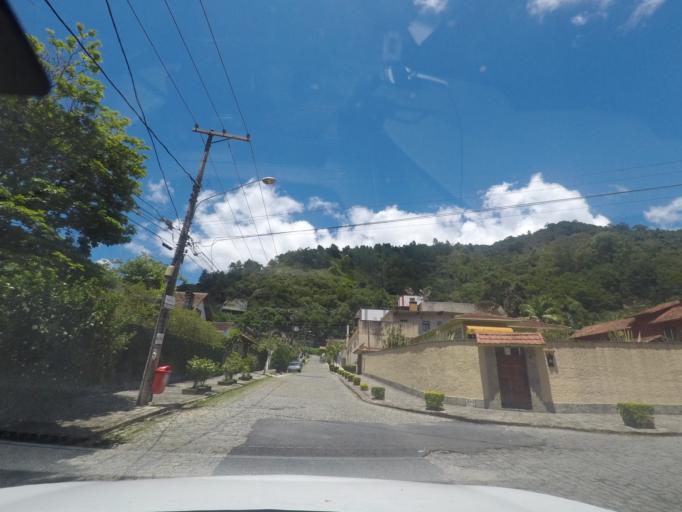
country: BR
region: Rio de Janeiro
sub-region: Teresopolis
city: Teresopolis
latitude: -22.4310
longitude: -42.9816
